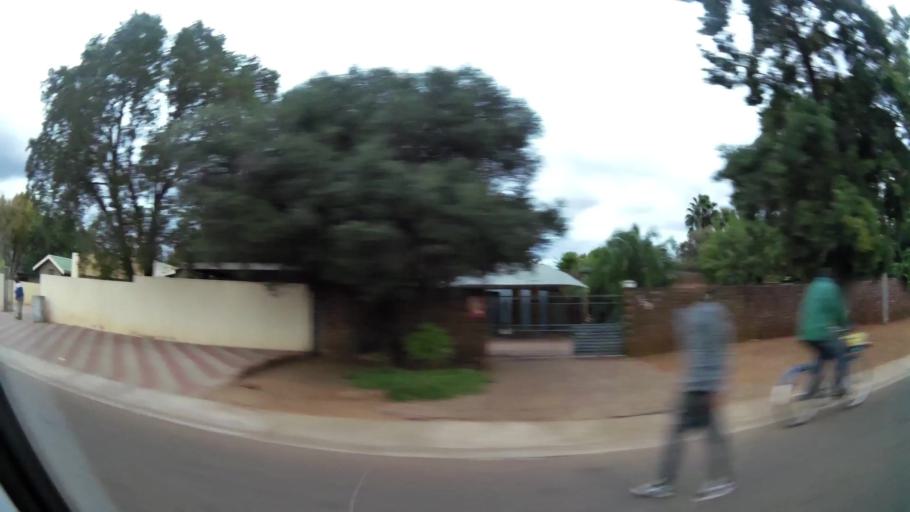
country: ZA
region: Limpopo
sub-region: Waterberg District Municipality
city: Mokopane
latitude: -24.1921
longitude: 28.9964
